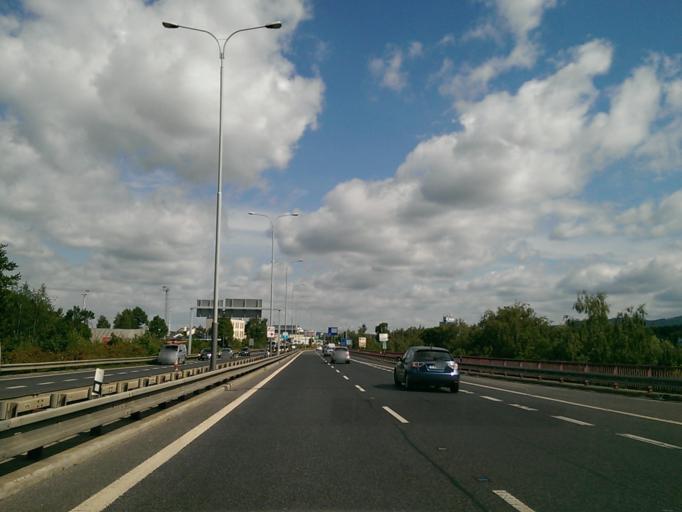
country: CZ
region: Liberecky
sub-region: Okres Liberec
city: Liberec
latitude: 50.7521
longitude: 15.0534
